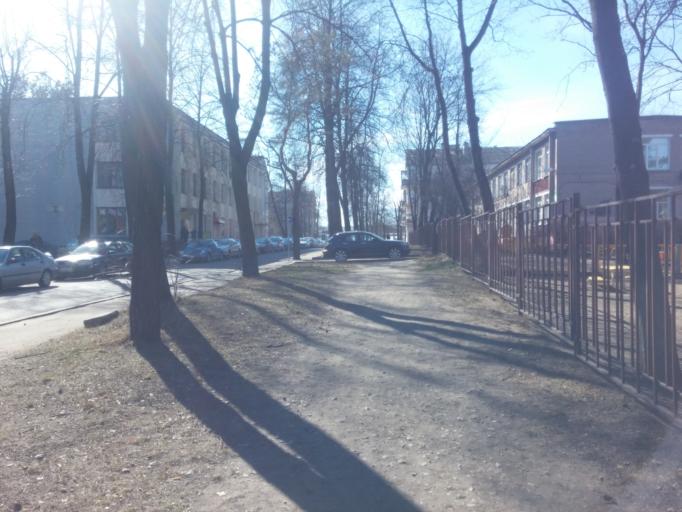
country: BY
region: Minsk
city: Vyaliki Trastsyanets
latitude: 53.8649
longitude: 27.6541
